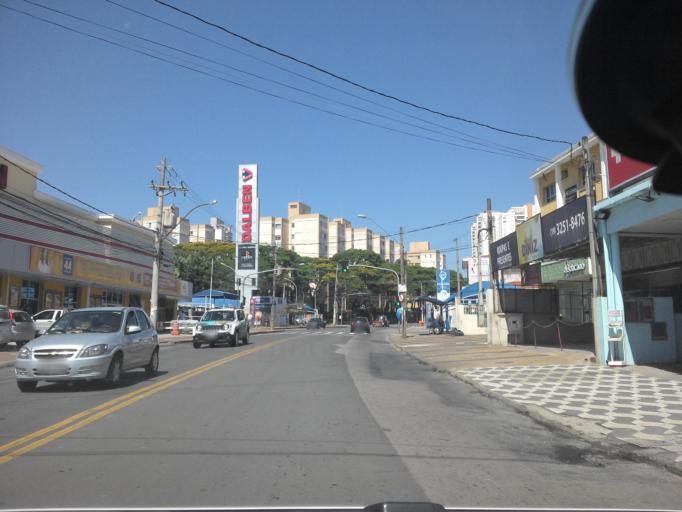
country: BR
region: Sao Paulo
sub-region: Campinas
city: Campinas
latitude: -22.8782
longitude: -47.0443
